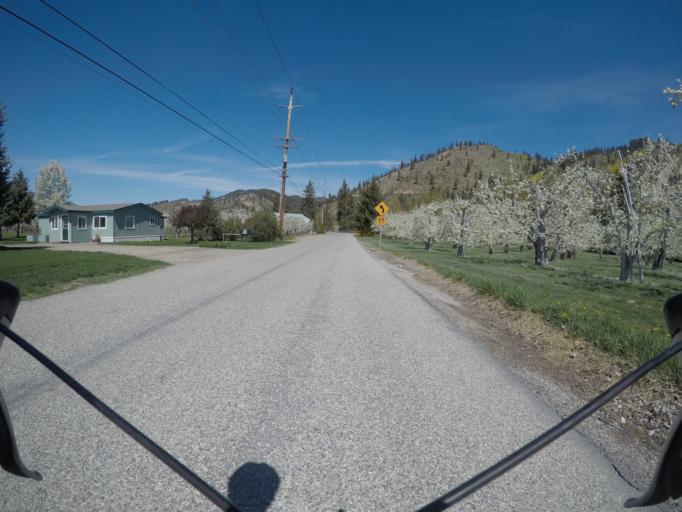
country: US
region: Washington
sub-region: Chelan County
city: Leavenworth
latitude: 47.5627
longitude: -120.5824
